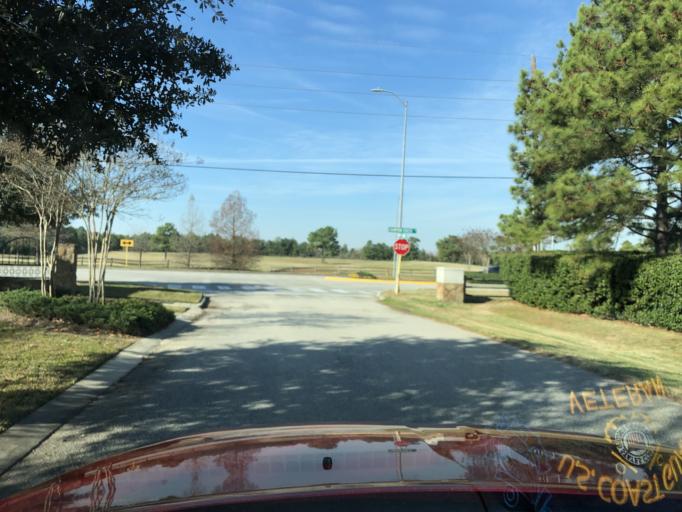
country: US
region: Texas
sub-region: Harris County
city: Tomball
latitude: 30.0406
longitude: -95.5620
